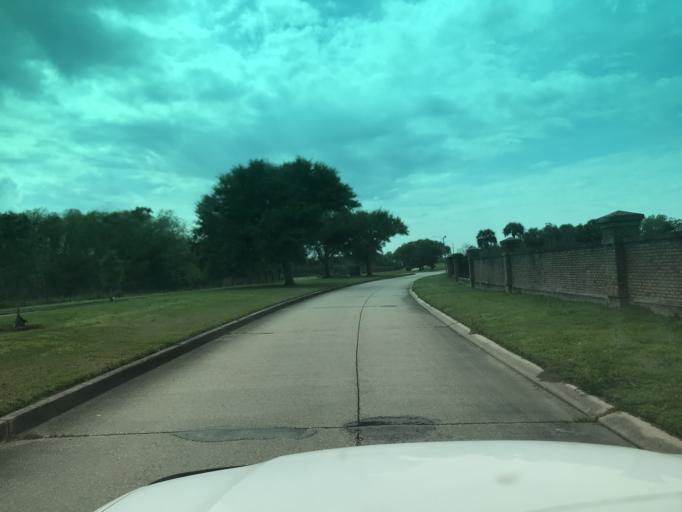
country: US
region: Louisiana
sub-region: Saint Bernard Parish
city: Chalmette
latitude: 30.0394
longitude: -89.9458
